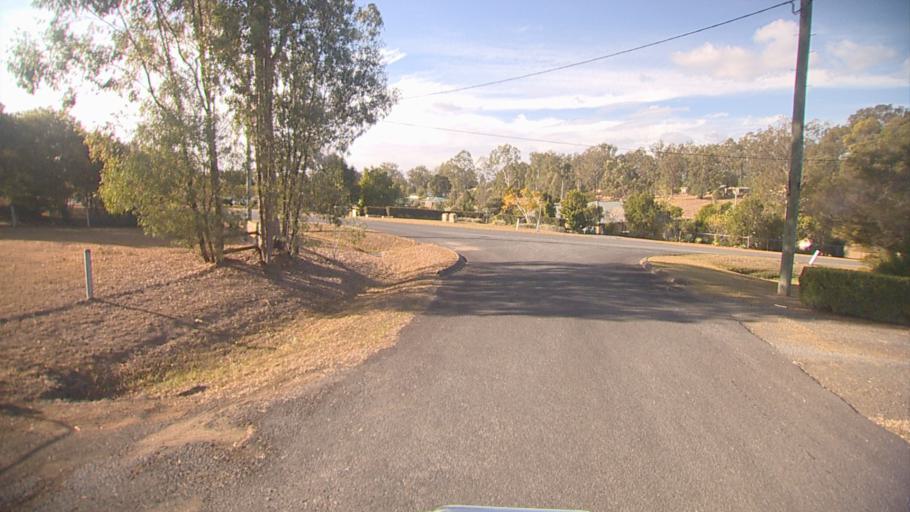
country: AU
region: Queensland
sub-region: Logan
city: Cedar Vale
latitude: -27.8757
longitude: 153.0066
